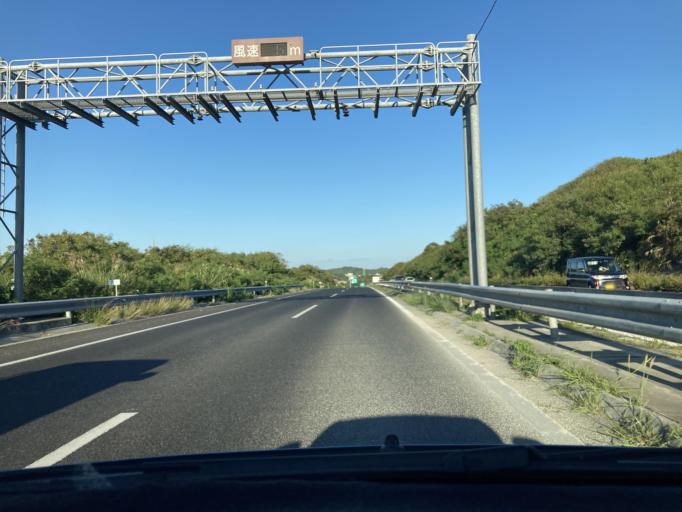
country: JP
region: Okinawa
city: Tomigusuku
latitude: 26.1755
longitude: 127.7063
